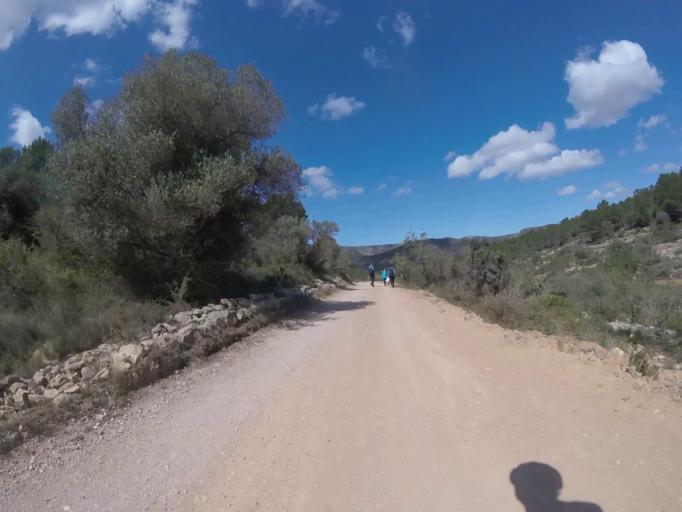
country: ES
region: Valencia
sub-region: Provincia de Castello
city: Santa Magdalena de Pulpis
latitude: 40.3232
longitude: 0.3485
